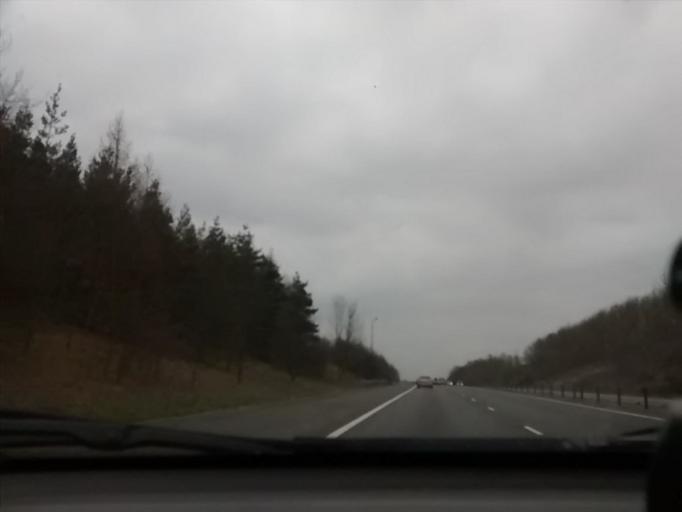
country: GB
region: England
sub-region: Essex
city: Saffron Walden
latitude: 51.9947
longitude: 0.1951
